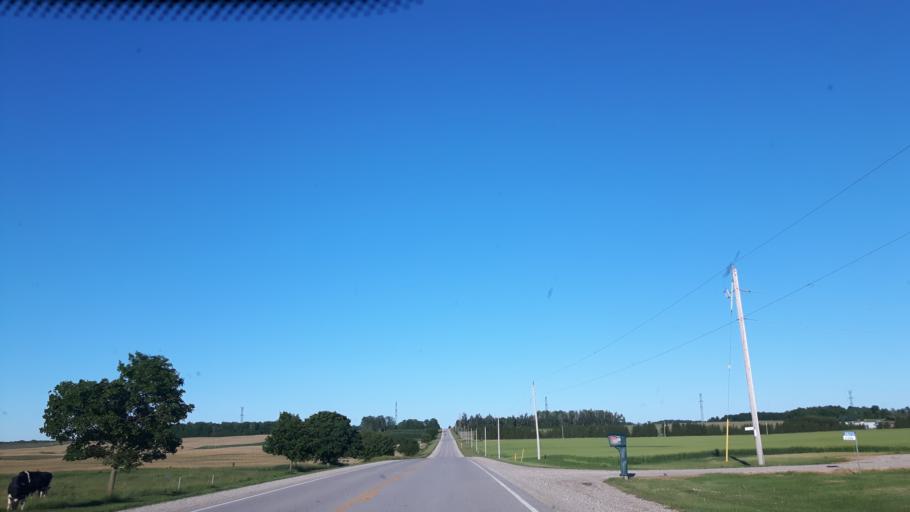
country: CA
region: Ontario
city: Goderich
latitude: 43.6427
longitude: -81.6511
